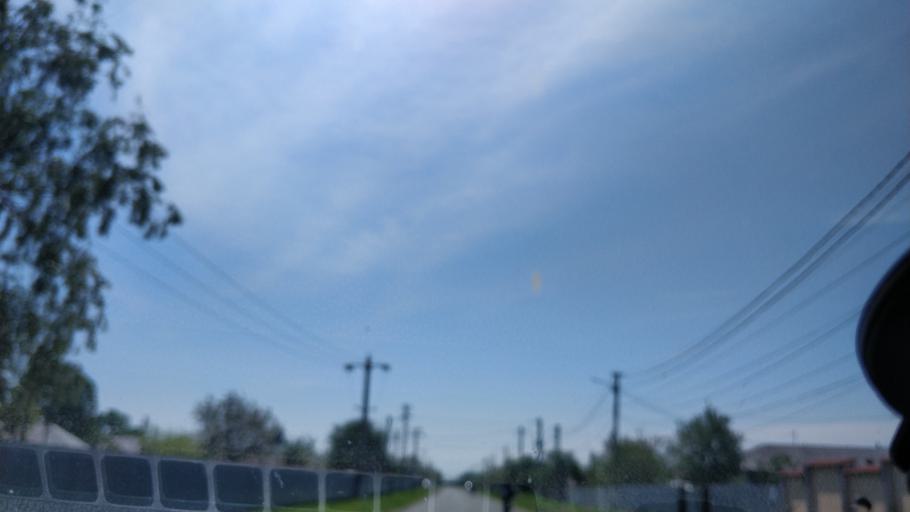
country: RO
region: Vrancea
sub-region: Comuna Suraia
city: Suraia
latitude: 45.6701
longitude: 27.3872
